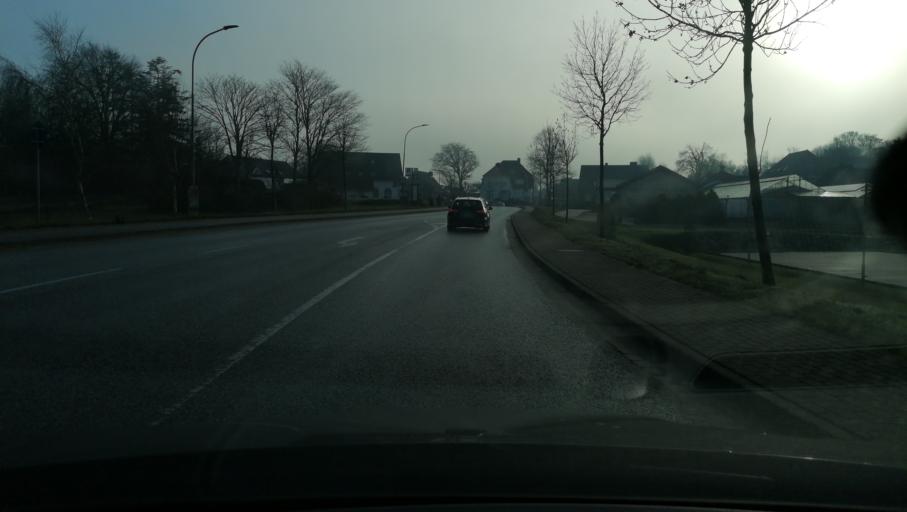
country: DE
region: Schleswig-Holstein
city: Meldorf
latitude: 54.0904
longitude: 9.0837
